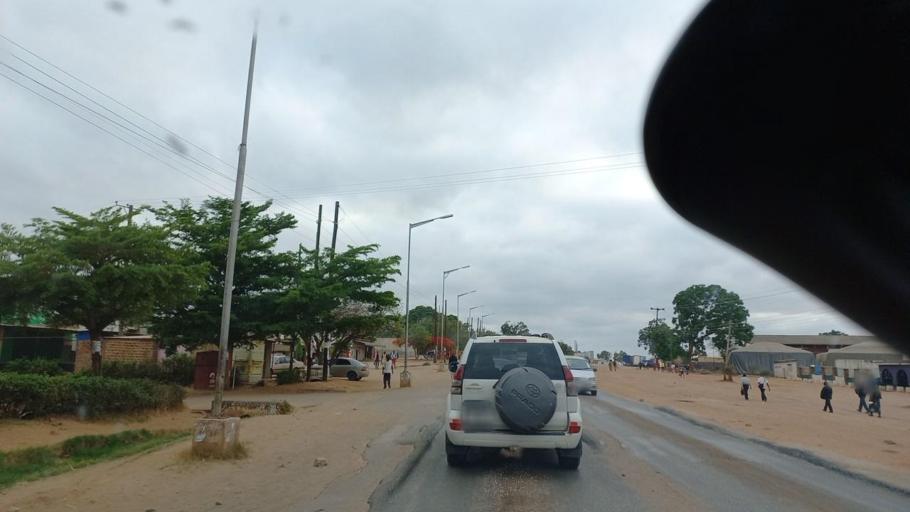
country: ZM
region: Lusaka
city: Chongwe
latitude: -15.3287
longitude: 28.6777
